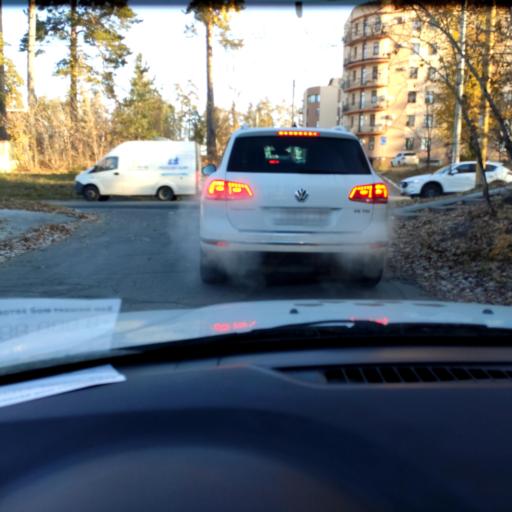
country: RU
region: Samara
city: Tol'yatti
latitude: 53.4753
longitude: 49.3735
